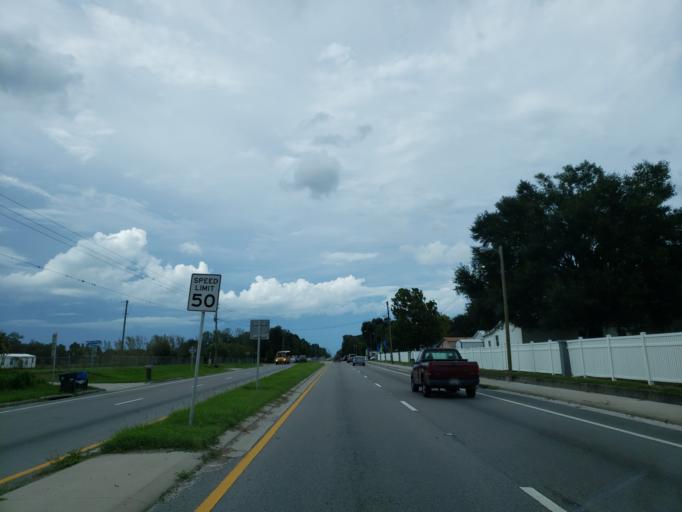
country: US
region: Florida
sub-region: Polk County
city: Willow Oak
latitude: 27.9283
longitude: -82.0552
